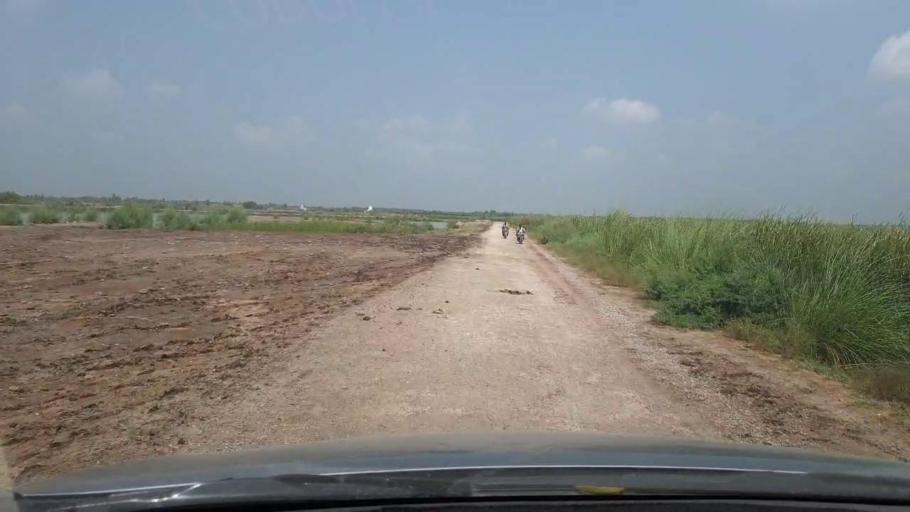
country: PK
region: Sindh
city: Khairpur
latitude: 27.4751
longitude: 68.7020
